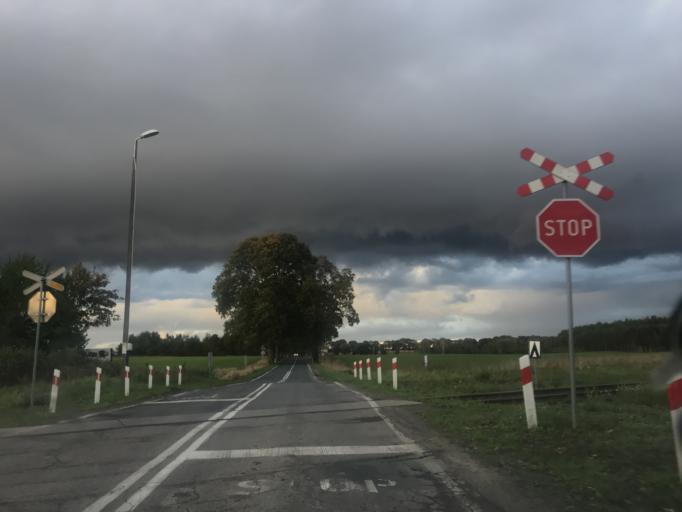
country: PL
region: West Pomeranian Voivodeship
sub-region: Powiat walecki
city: Tuczno
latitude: 53.2187
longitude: 16.1723
